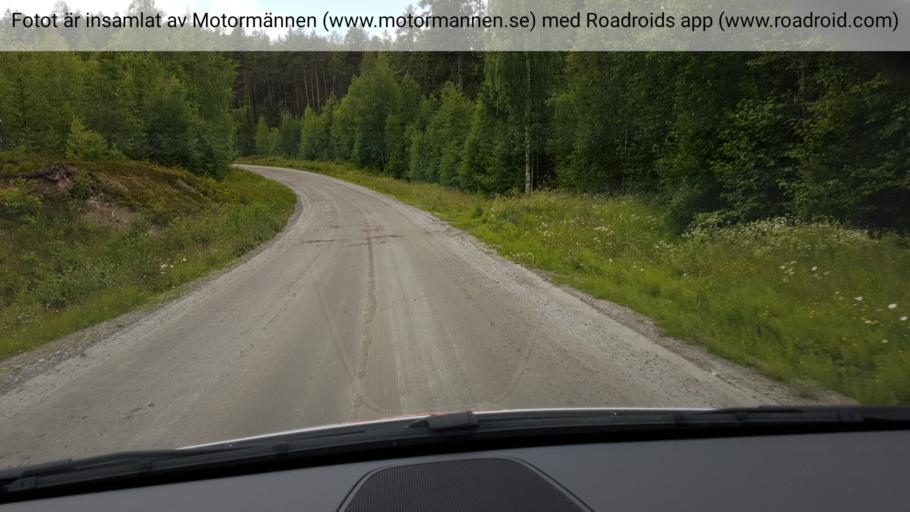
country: SE
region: Vaesterbotten
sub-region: Dorotea Kommun
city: Dorotea
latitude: 63.9221
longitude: 16.2539
